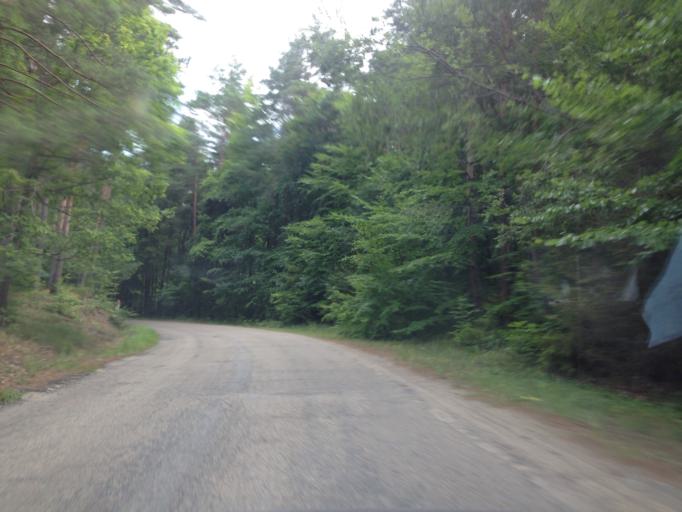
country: PL
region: Pomeranian Voivodeship
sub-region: Powiat koscierski
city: Lipusz
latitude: 54.0780
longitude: 17.7559
